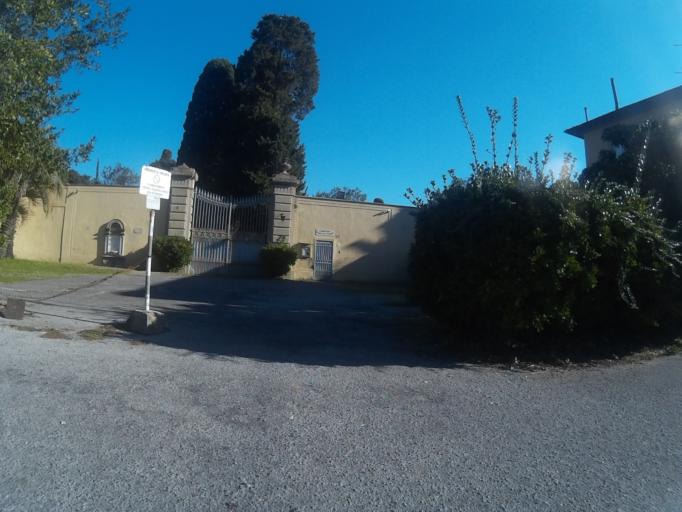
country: IT
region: Tuscany
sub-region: Provincia di Livorno
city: Livorno
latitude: 43.5687
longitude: 10.3270
